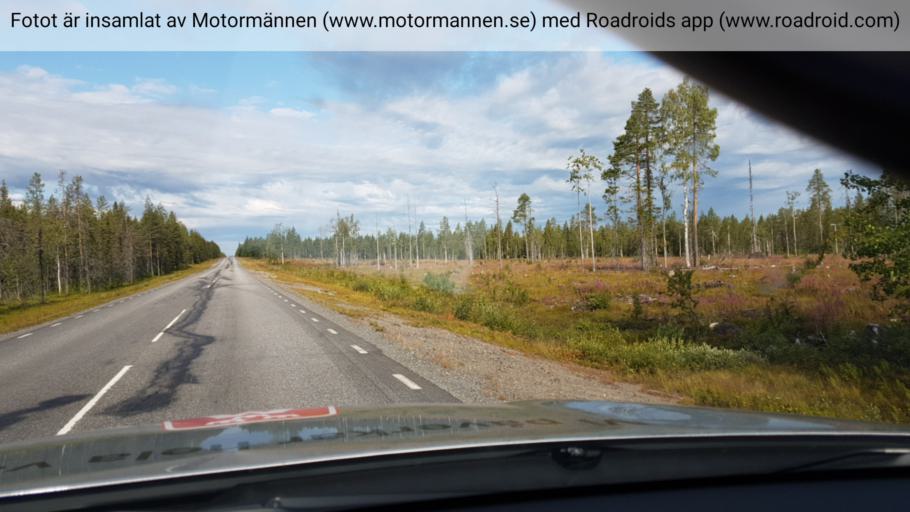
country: SE
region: Vaesterbotten
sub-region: Skelleftea Kommun
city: Storvik
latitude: 65.3516
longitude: 20.4900
